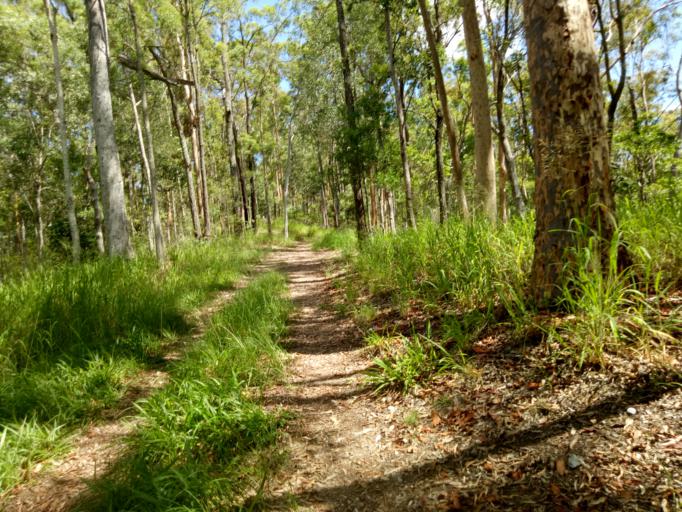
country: AU
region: Queensland
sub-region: Moreton Bay
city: Ferny Hills
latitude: -27.4460
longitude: 152.9103
